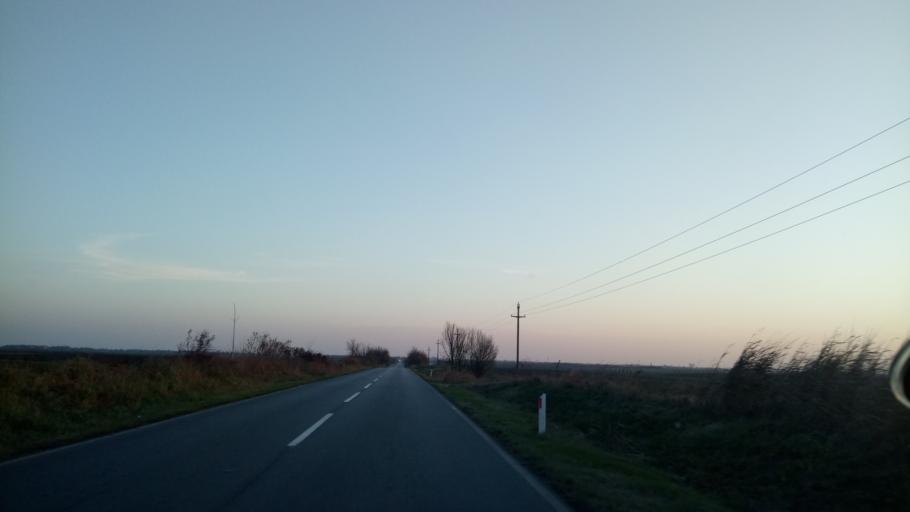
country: RS
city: Surduk
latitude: 45.0502
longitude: 20.3320
